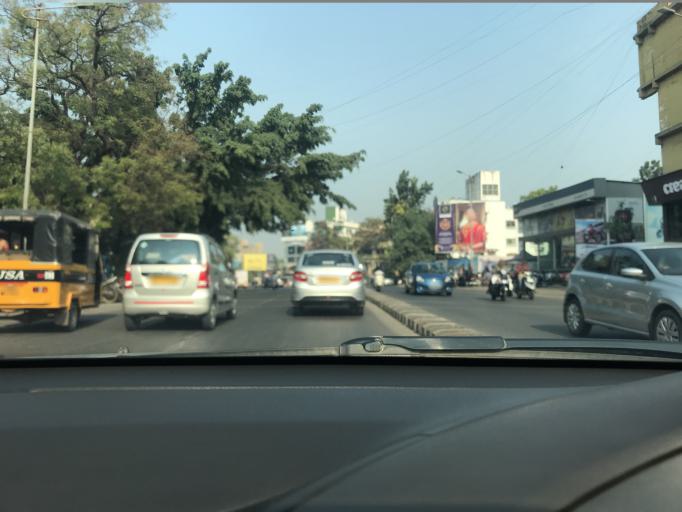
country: IN
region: Maharashtra
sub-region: Pune Division
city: Khadki
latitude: 18.5532
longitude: 73.8027
